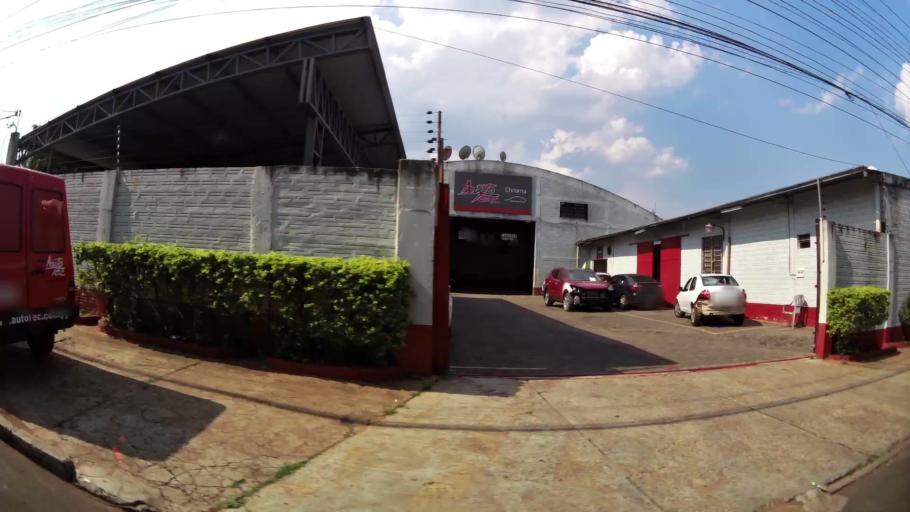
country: PY
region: Alto Parana
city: Ciudad del Este
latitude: -25.5033
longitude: -54.6316
